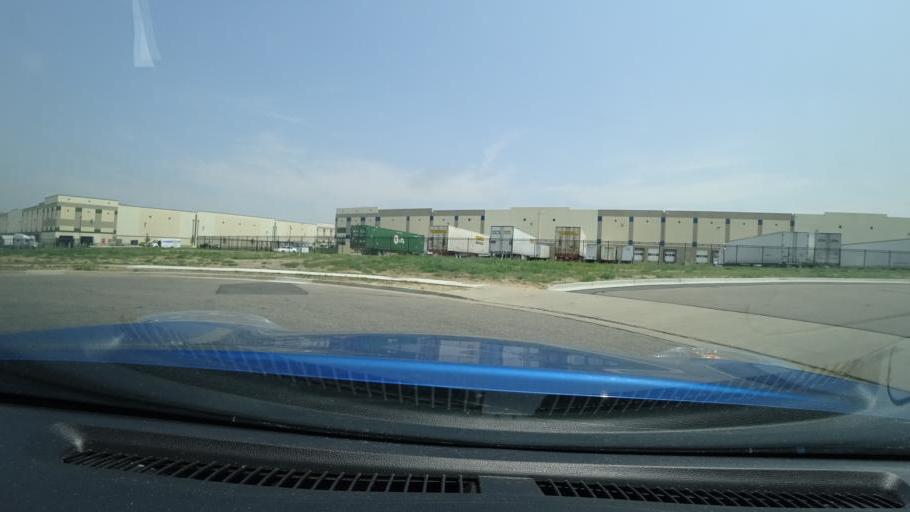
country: US
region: Colorado
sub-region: Adams County
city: Aurora
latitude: 39.7611
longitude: -104.7571
